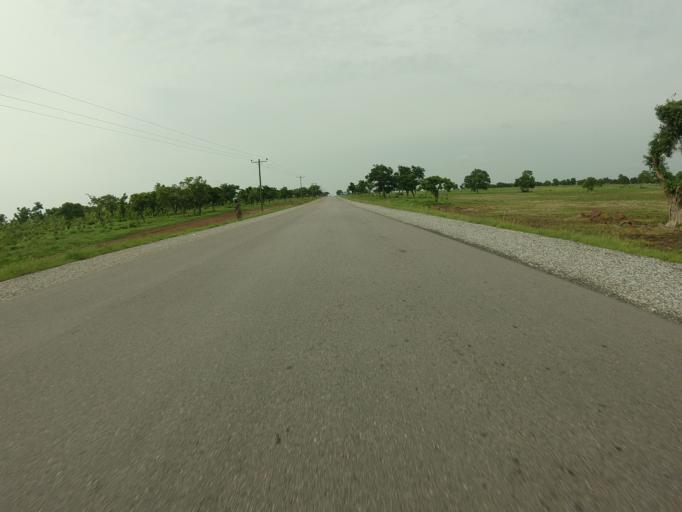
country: GH
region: Northern
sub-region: Yendi
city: Yendi
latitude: 9.8171
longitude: -0.1172
